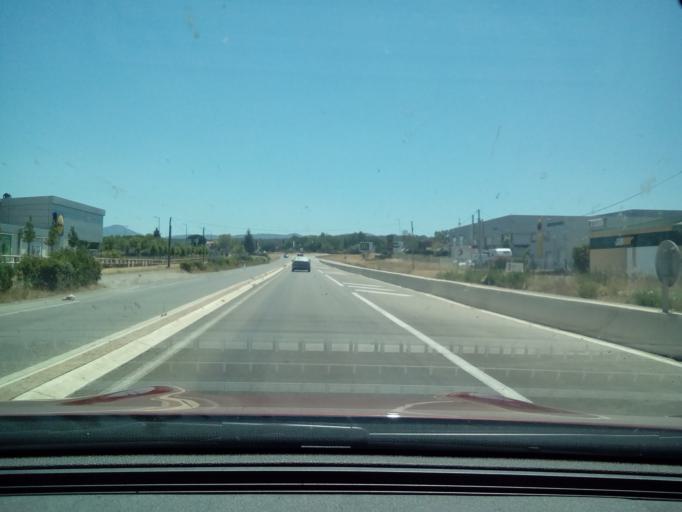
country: FR
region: Provence-Alpes-Cote d'Azur
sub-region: Departement des Bouches-du-Rhone
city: Rousset
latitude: 43.4656
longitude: 5.6070
